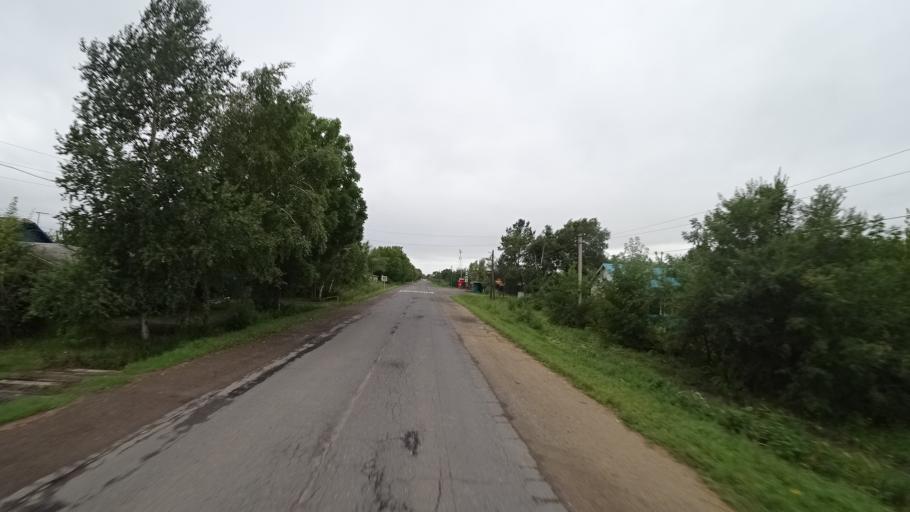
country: RU
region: Primorskiy
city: Chernigovka
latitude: 44.3470
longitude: 132.5578
